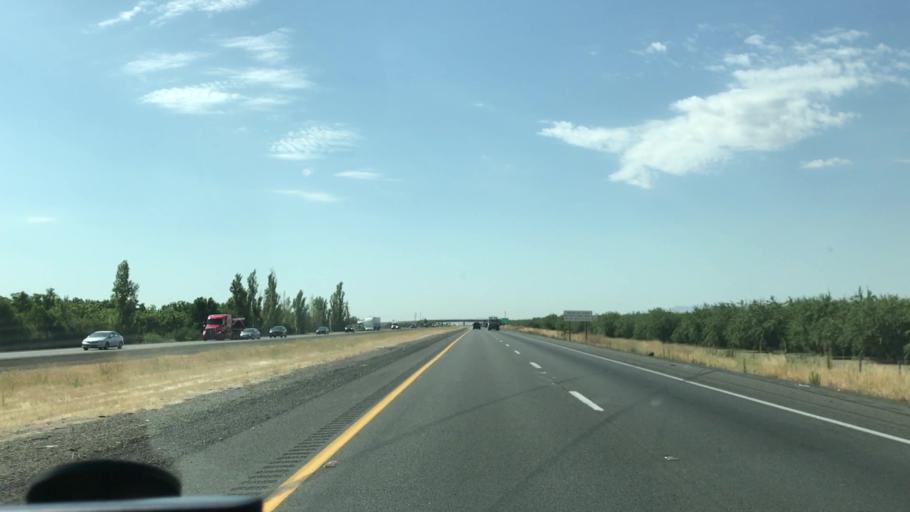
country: US
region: California
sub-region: Merced County
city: Gustine
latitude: 37.1395
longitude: -121.0387
